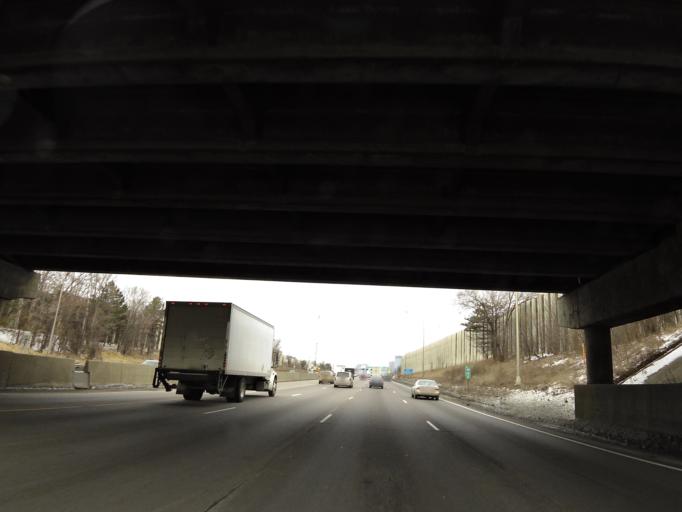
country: US
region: Minnesota
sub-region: Hennepin County
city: Minneapolis
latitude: 44.9394
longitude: -93.2745
